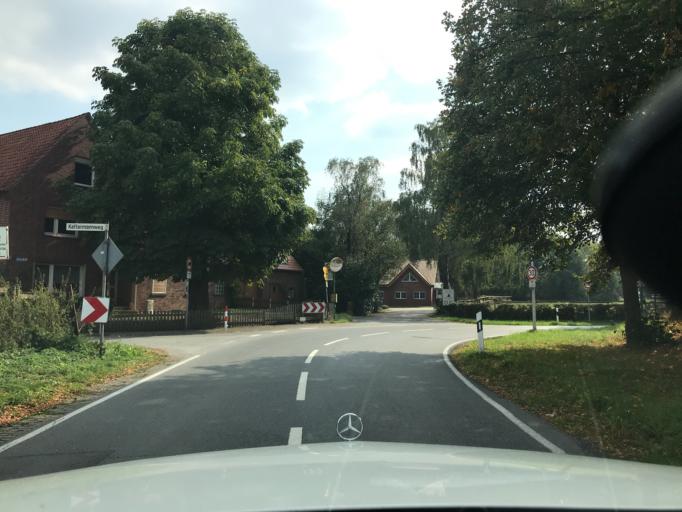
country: DE
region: North Rhine-Westphalia
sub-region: Regierungsbezirk Arnsberg
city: Werl
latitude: 51.6035
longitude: 7.8759
